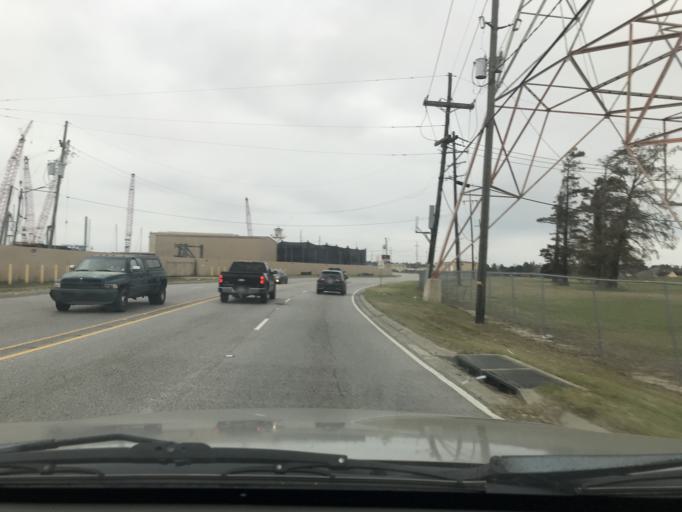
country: US
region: Louisiana
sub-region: Jefferson Parish
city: Harvey
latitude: 29.8832
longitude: -90.0759
